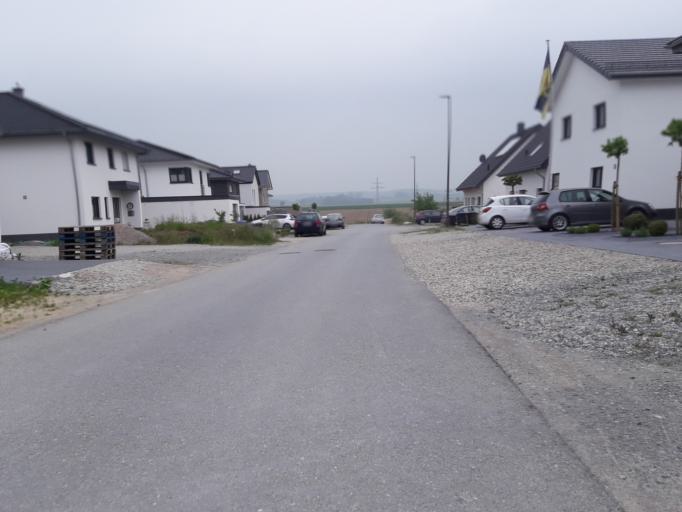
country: DE
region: North Rhine-Westphalia
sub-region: Regierungsbezirk Detmold
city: Salzkotten
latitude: 51.6675
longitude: 8.6268
